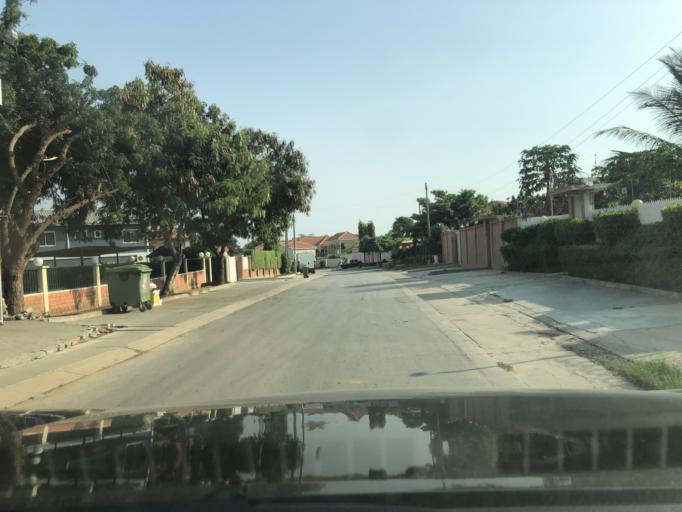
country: AO
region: Luanda
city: Luanda
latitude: -8.9081
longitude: 13.2274
